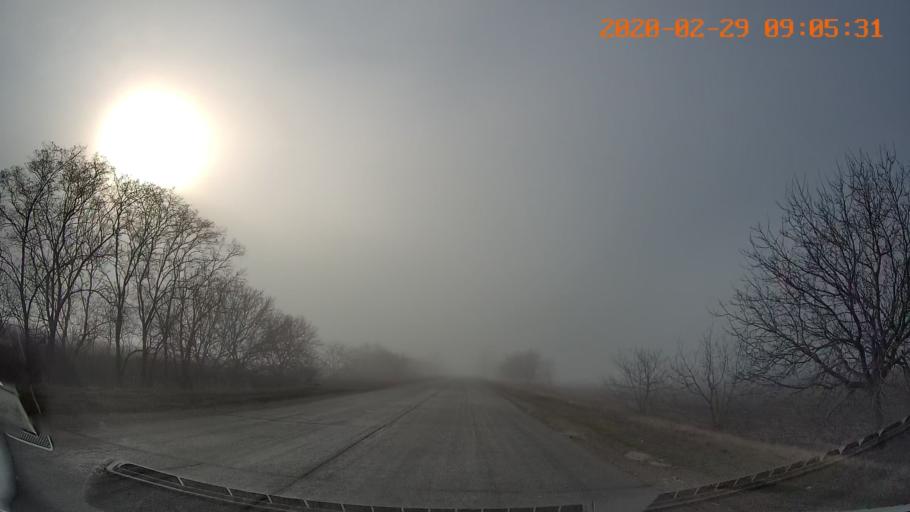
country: MD
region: Telenesti
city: Tiraspolul Nou
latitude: 46.8882
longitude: 29.7406
